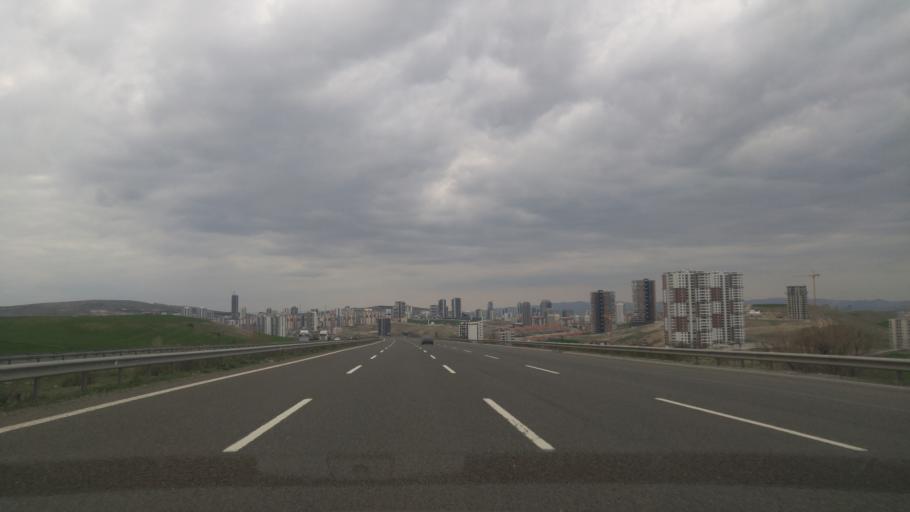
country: TR
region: Ankara
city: Etimesgut
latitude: 39.8287
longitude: 32.6463
